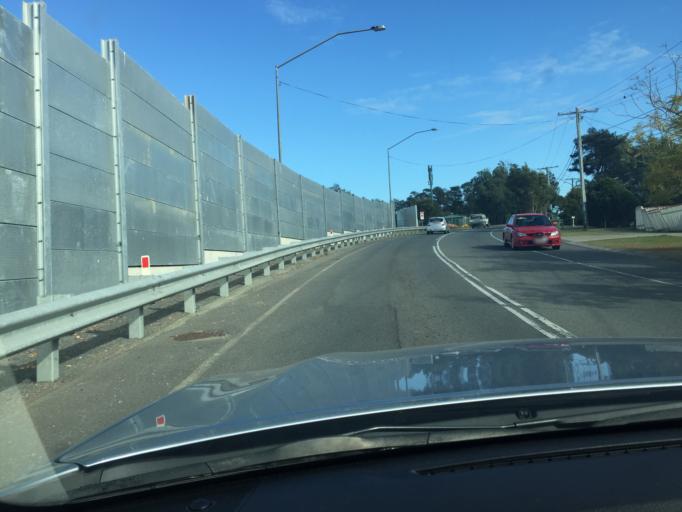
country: AU
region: Queensland
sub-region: Logan
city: Slacks Creek
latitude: -27.6465
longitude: 153.1510
